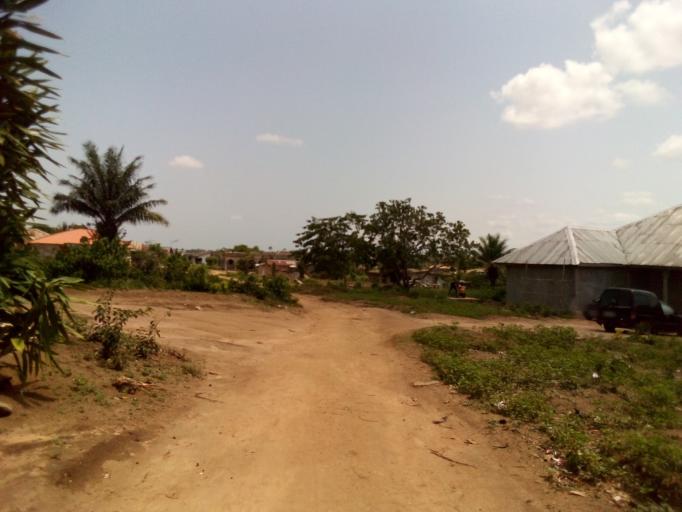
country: SL
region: Western Area
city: Waterloo
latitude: 8.3422
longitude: -13.0240
